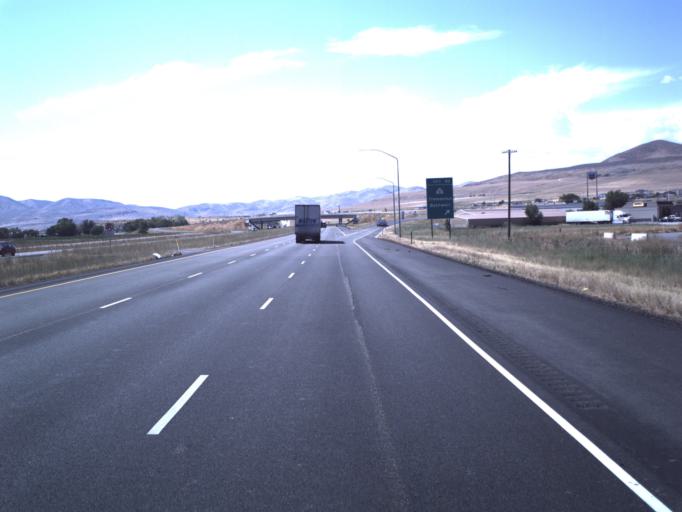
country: US
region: Utah
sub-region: Box Elder County
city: Tremonton
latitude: 41.7080
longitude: -112.1993
